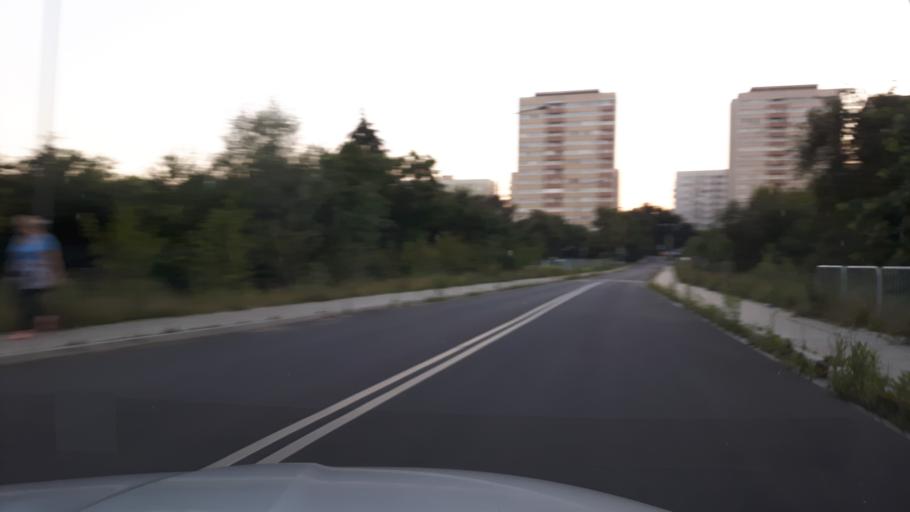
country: PL
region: Masovian Voivodeship
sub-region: Warszawa
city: Mokotow
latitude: 52.2053
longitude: 21.0547
